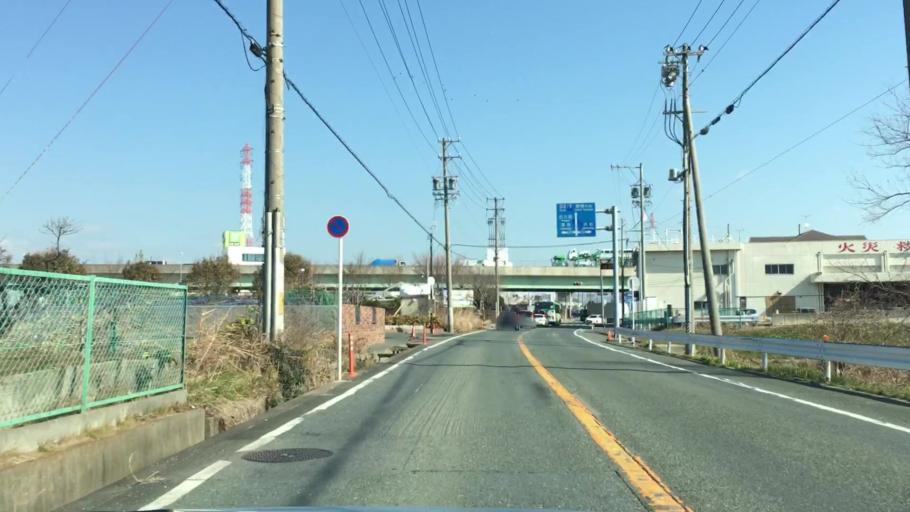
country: JP
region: Aichi
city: Toyohashi
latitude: 34.7057
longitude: 137.3531
